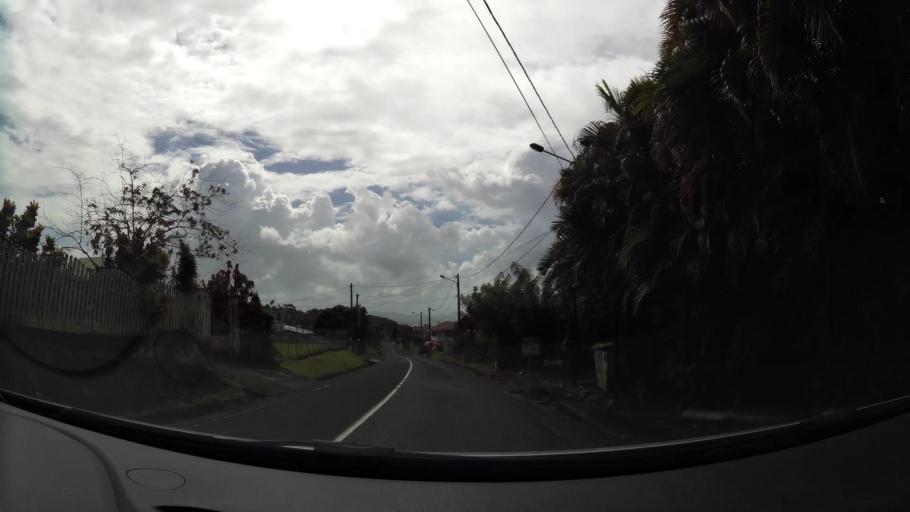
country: MQ
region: Martinique
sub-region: Martinique
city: Saint-Joseph
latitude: 14.6467
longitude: -61.0443
